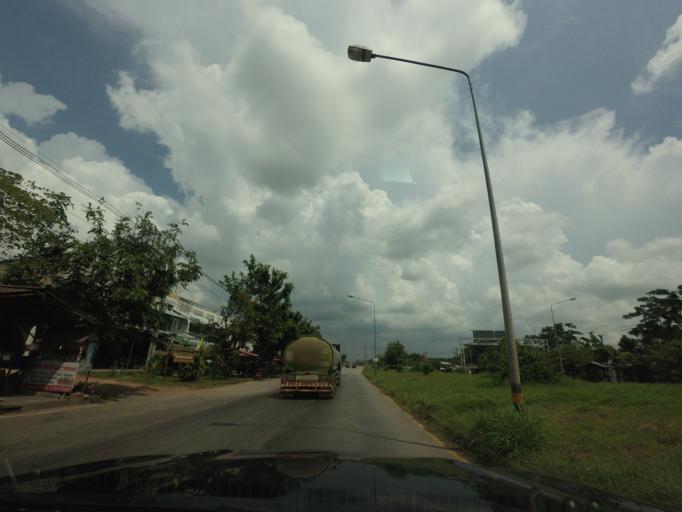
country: TH
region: Khon Kaen
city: Nong Ruea
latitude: 16.4906
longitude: 102.4059
